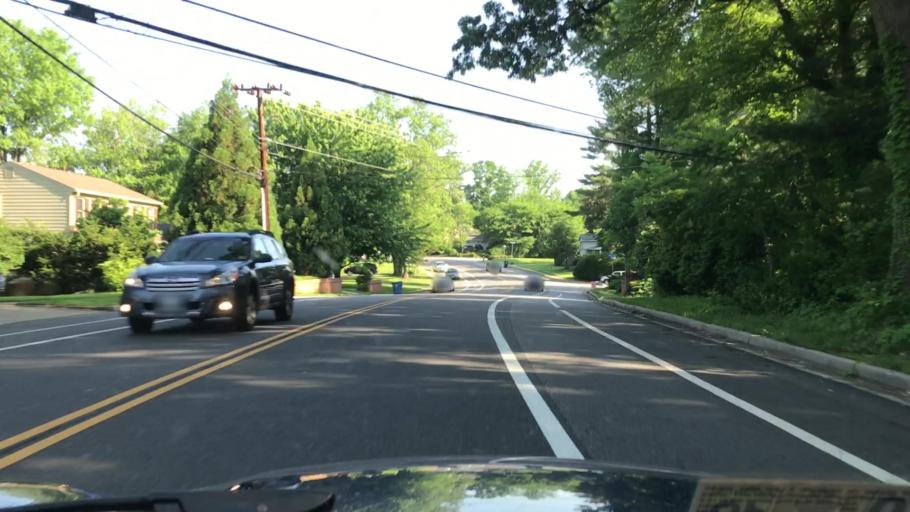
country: US
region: Virginia
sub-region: Fairfax County
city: Kings Park
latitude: 38.8183
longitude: -77.2363
